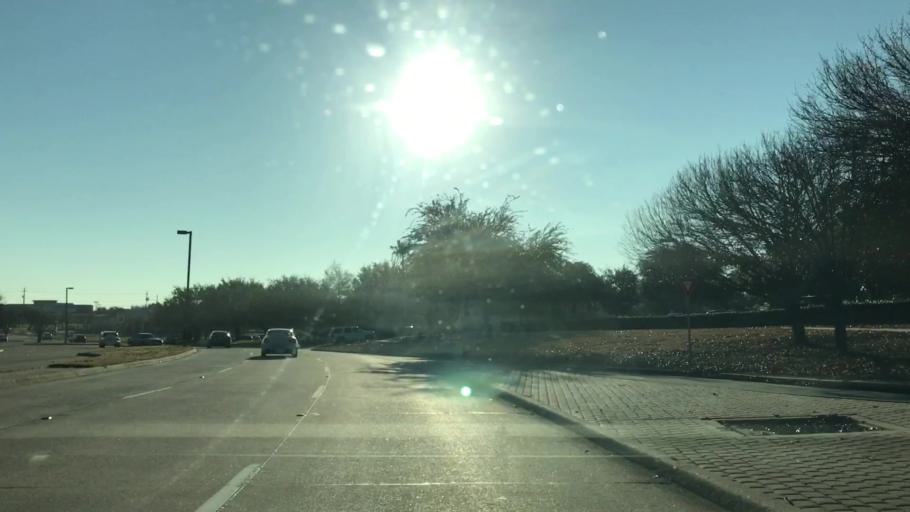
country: US
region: Texas
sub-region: Dallas County
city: Coppell
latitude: 32.9210
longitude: -96.9977
